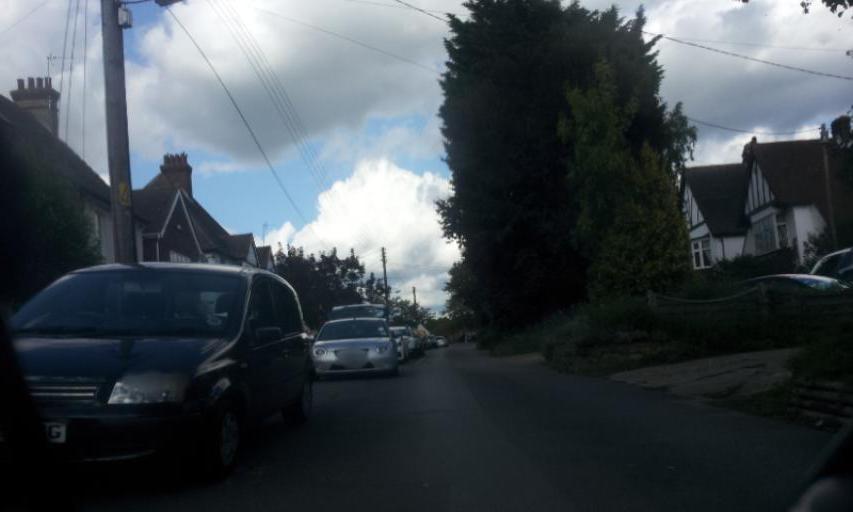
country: GB
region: England
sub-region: Kent
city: Snodland
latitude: 51.3258
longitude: 0.4322
